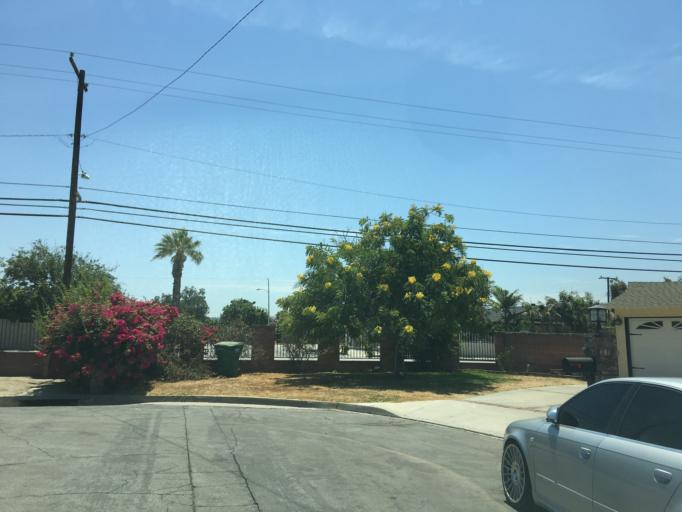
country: US
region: California
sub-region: Los Angeles County
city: Charter Oak
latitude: 34.1035
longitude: -117.8534
